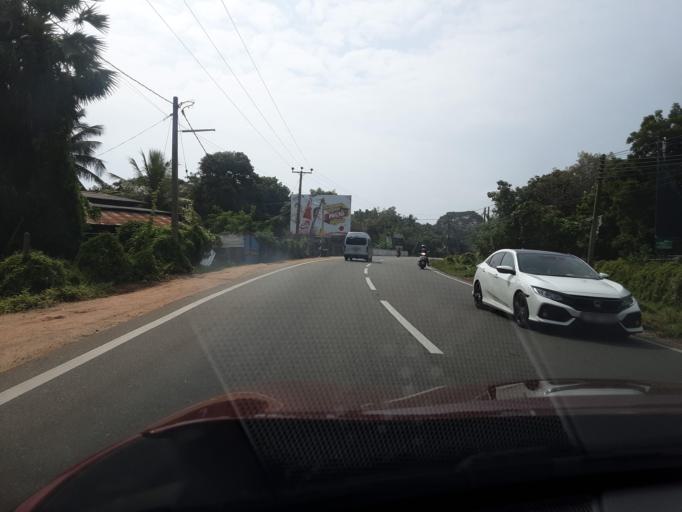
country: LK
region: Northern Province
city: Jaffna
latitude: 9.6607
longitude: 80.0489
